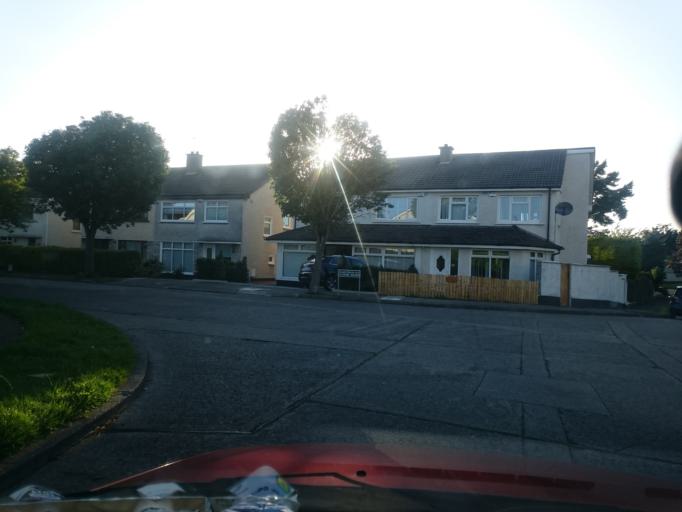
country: IE
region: Leinster
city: Balally
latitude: 53.2775
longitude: -6.2362
